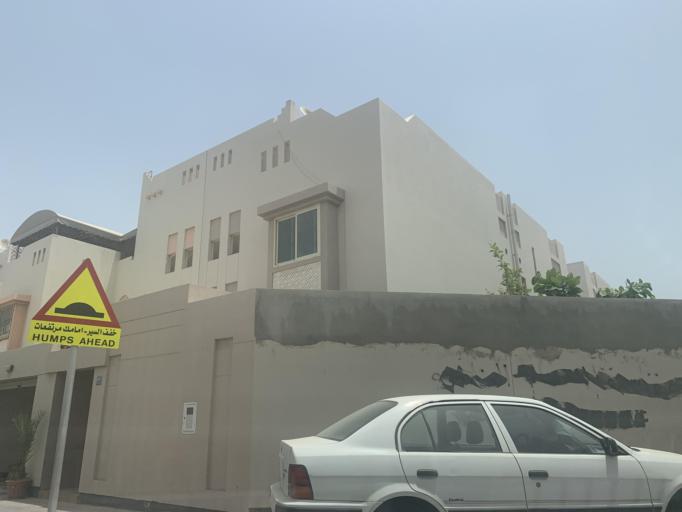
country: BH
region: Manama
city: Jidd Hafs
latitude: 26.2103
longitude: 50.5377
